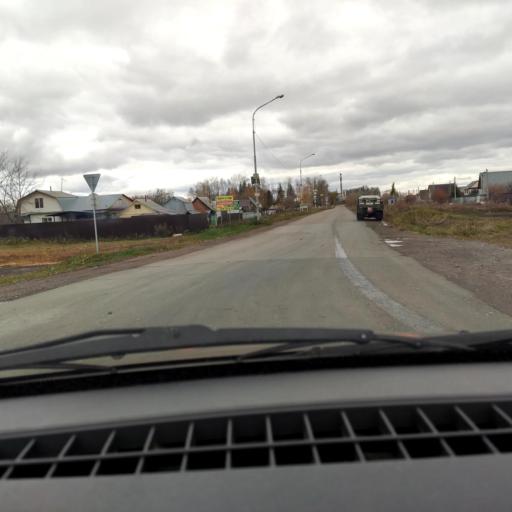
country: RU
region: Bashkortostan
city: Ufa
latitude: 54.5732
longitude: 55.9075
